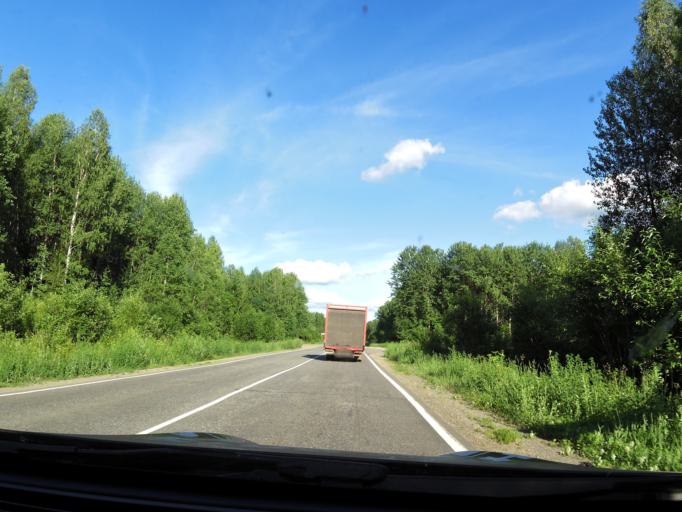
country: RU
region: Kirov
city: Omutninsk
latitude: 58.7683
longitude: 51.9684
